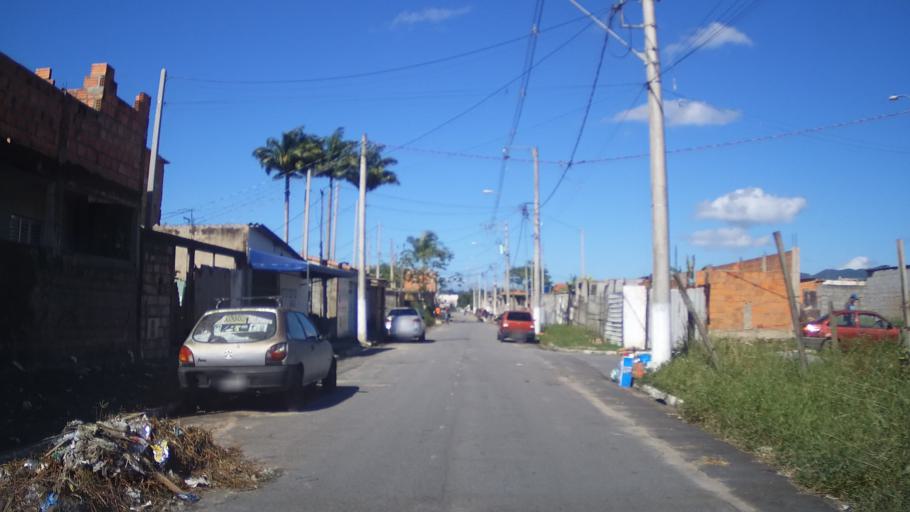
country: BR
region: Sao Paulo
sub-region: Praia Grande
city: Praia Grande
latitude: -24.0235
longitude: -46.5214
